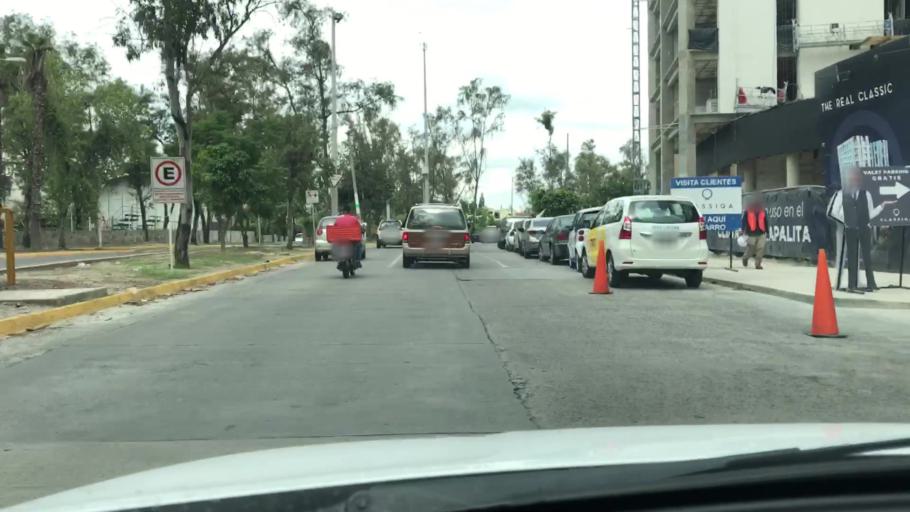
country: MX
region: Jalisco
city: Guadalajara
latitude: 20.6587
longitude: -103.4320
